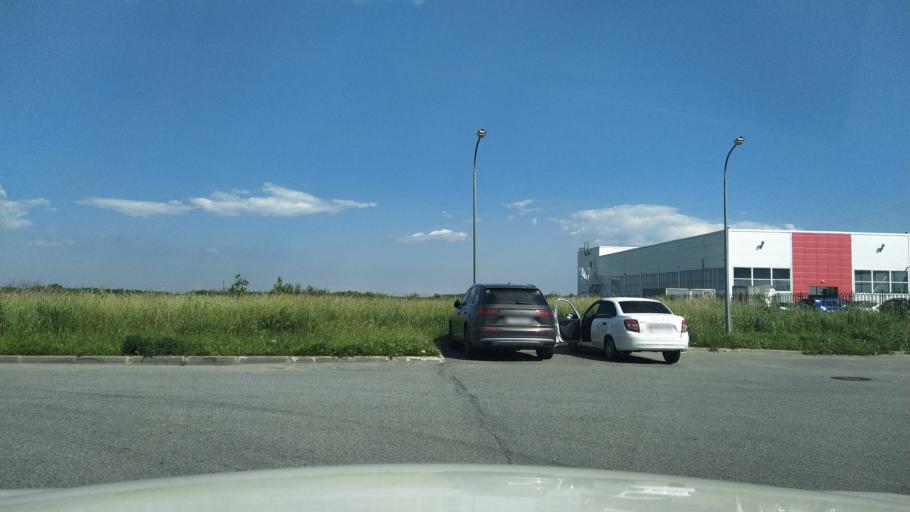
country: RU
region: St.-Petersburg
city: Aleksandrovskaya
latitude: 59.7836
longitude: 30.3273
